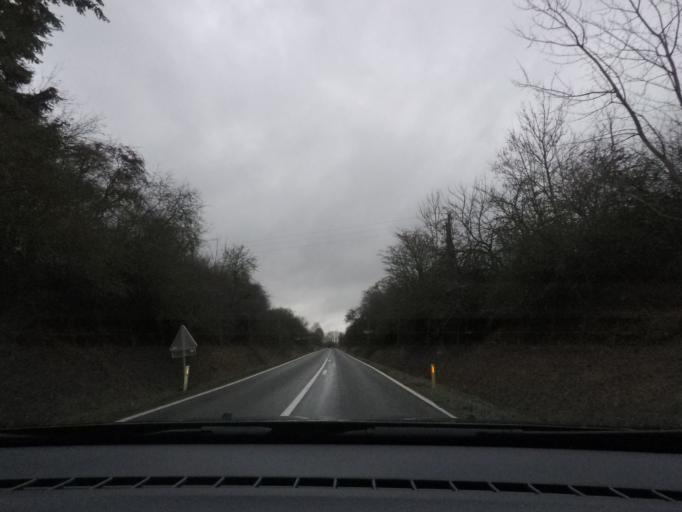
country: BE
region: Wallonia
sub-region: Province du Luxembourg
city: Tintigny
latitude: 49.6972
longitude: 5.5285
